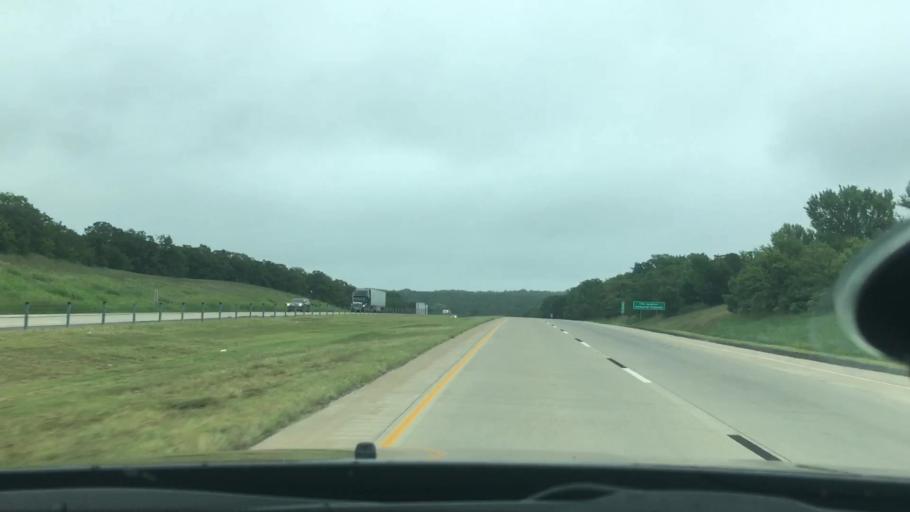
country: US
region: Oklahoma
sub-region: Okmulgee County
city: Henryetta
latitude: 35.4311
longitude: -95.9646
